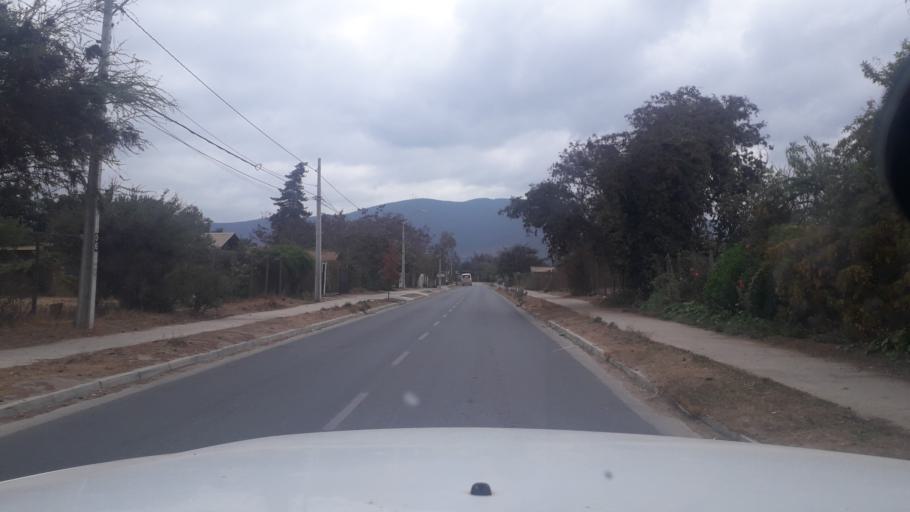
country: CL
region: Valparaiso
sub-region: Provincia de Marga Marga
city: Limache
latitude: -33.0166
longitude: -71.2685
